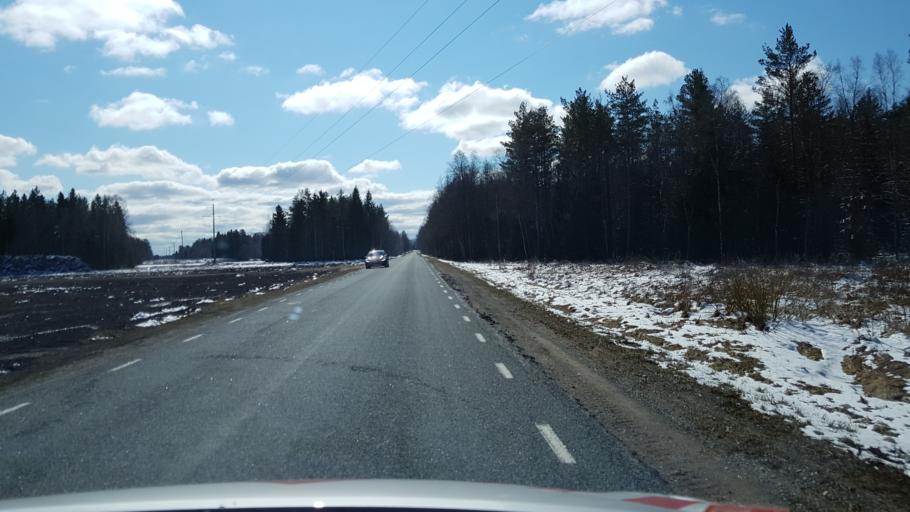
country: EE
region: Laeaene-Virumaa
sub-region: Kadrina vald
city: Kadrina
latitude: 59.4812
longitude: 25.9943
